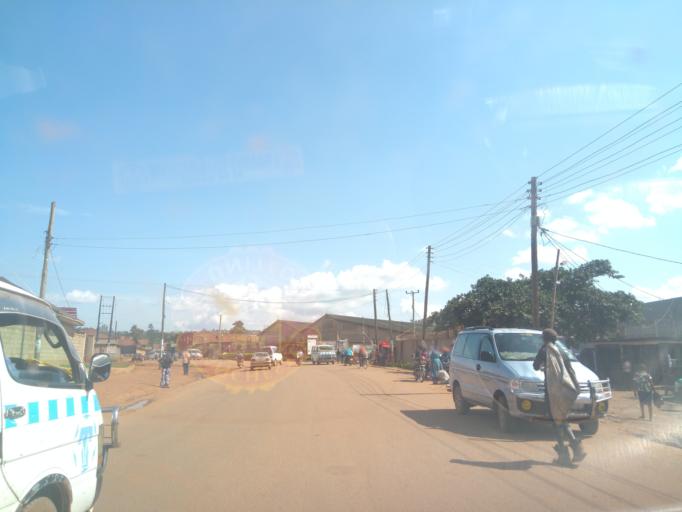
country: UG
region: Central Region
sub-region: Kampala District
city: Kampala
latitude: 0.2892
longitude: 32.5482
